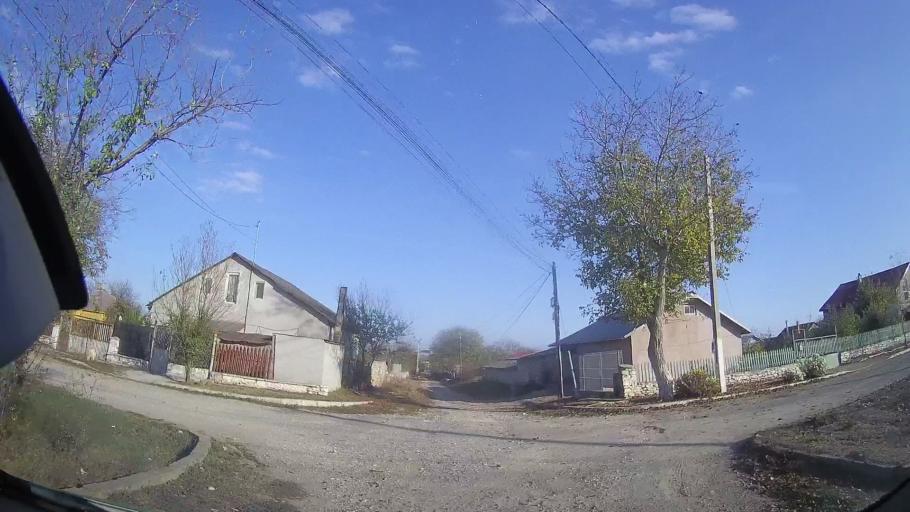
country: RO
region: Constanta
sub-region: Comuna Limanu
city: Limanu
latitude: 43.7967
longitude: 28.5301
